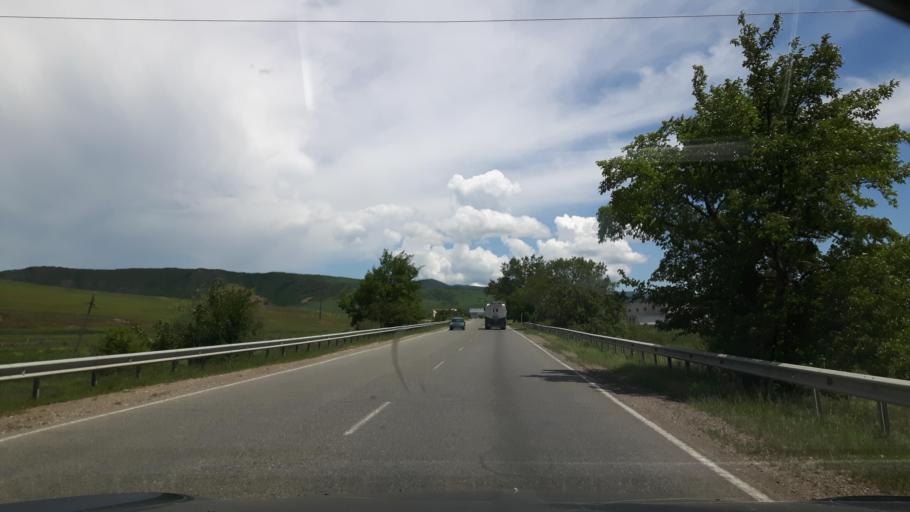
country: GE
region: Kakheti
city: Sagarejo
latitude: 41.7280
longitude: 45.1906
